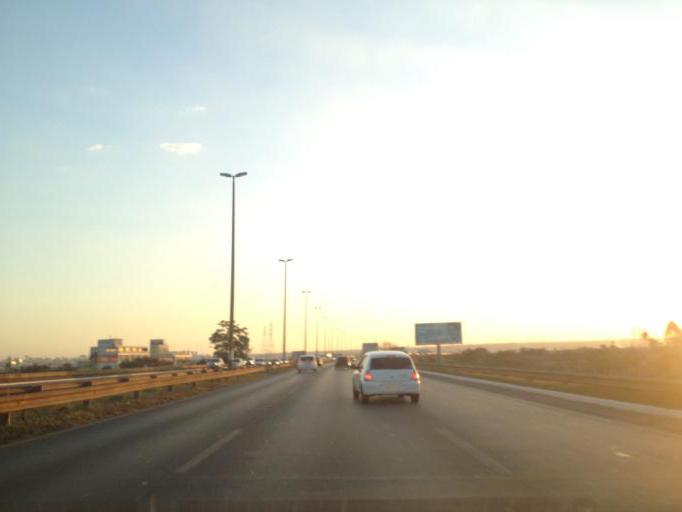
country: BR
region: Federal District
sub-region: Brasilia
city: Brasilia
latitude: -15.7950
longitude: -47.9627
